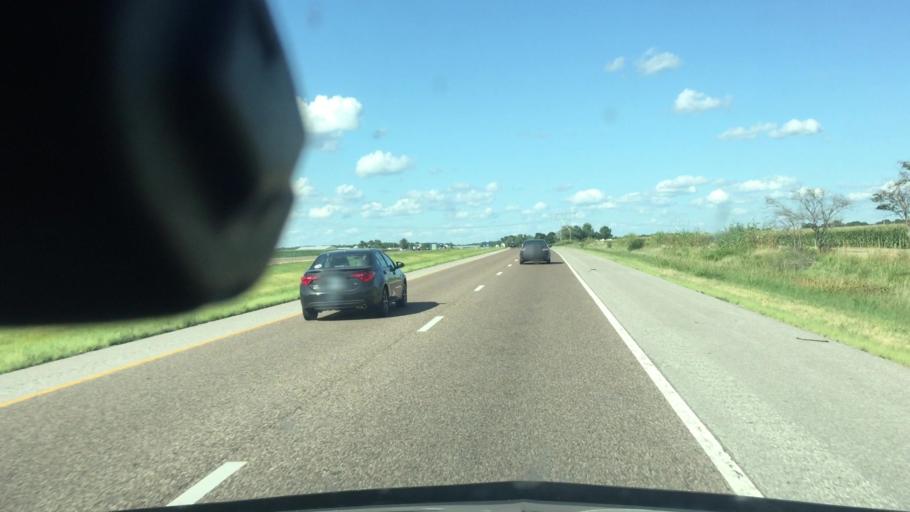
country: US
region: Illinois
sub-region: Madison County
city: Worden
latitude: 38.9398
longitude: -89.7901
